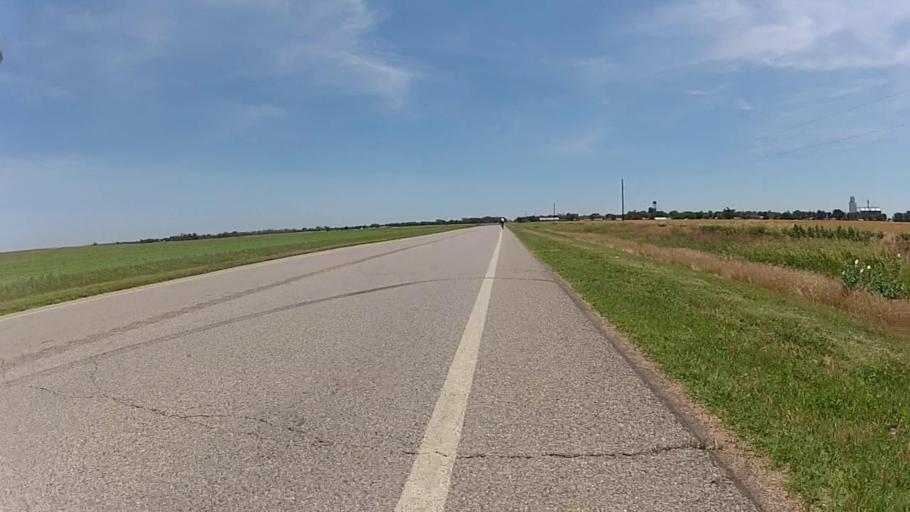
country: US
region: Kansas
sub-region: Barber County
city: Medicine Lodge
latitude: 37.2534
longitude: -98.4292
